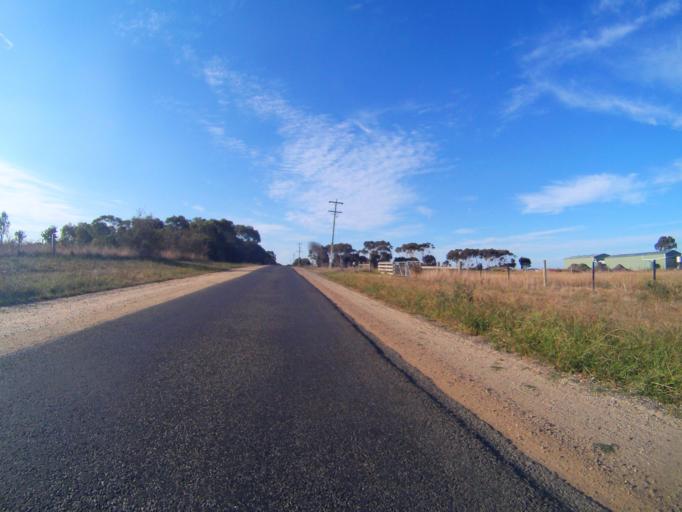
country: AU
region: Victoria
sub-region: Greater Geelong
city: Leopold
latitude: -38.2558
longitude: 144.4252
